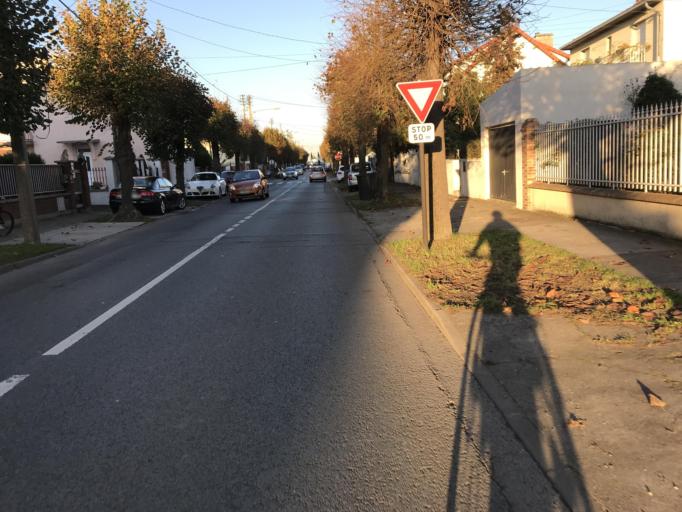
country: FR
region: Ile-de-France
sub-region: Departement de l'Essonne
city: Paray-Vieille-Poste
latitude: 48.7151
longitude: 2.3653
